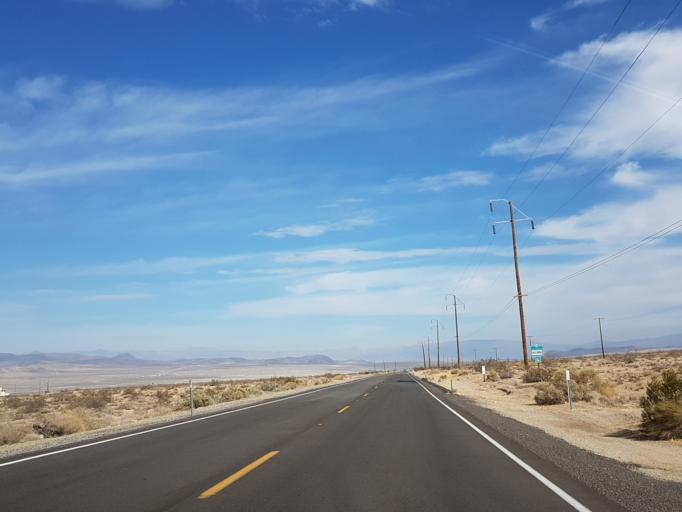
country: US
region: California
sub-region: Kern County
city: Ridgecrest
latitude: 35.6373
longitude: -117.5691
